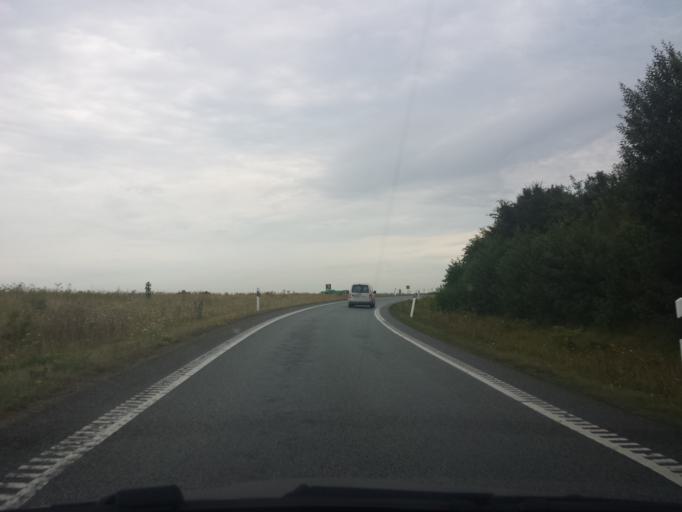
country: SE
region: Skane
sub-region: Malmo
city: Oxie
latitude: 55.5584
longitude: 13.0804
